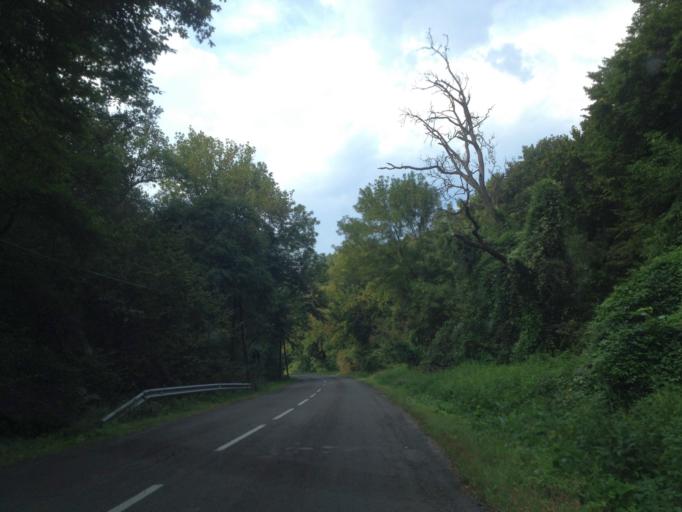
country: HU
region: Komarom-Esztergom
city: Kesztolc
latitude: 47.7423
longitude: 18.8074
